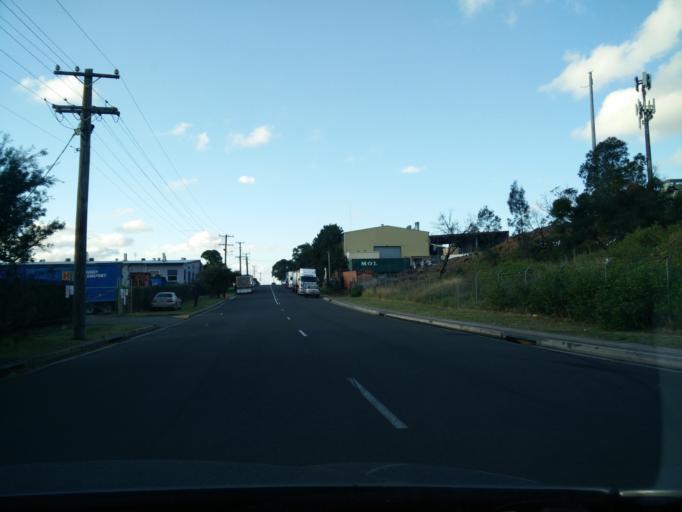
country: AU
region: New South Wales
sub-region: Wollongong
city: Cordeaux Heights
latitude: -34.4608
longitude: 150.8443
